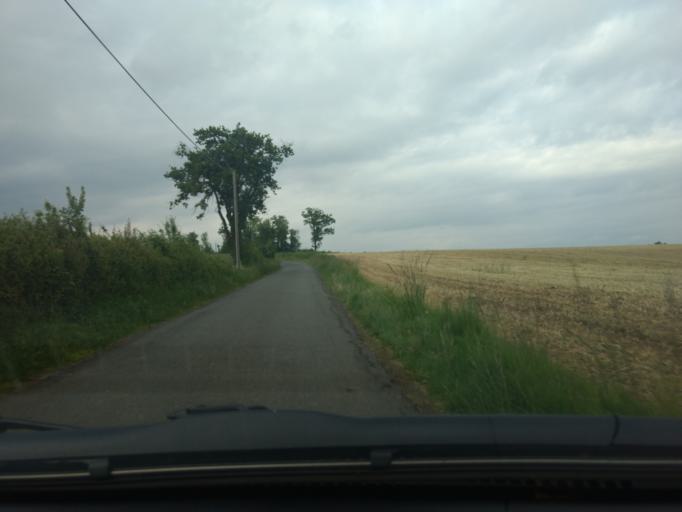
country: FR
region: Midi-Pyrenees
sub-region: Departement de l'Aveyron
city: Capdenac-Gare
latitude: 44.5444
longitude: 2.1216
